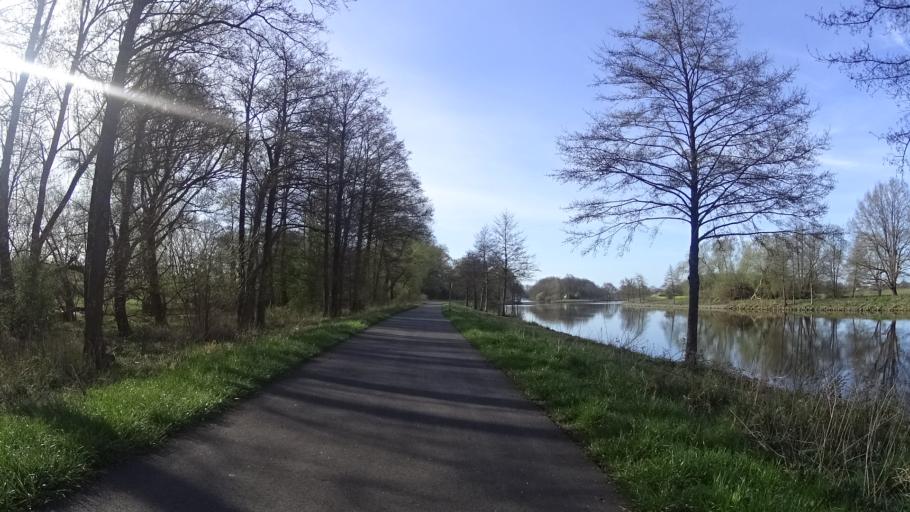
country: DE
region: Lower Saxony
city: Haren
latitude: 52.8010
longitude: 7.2616
